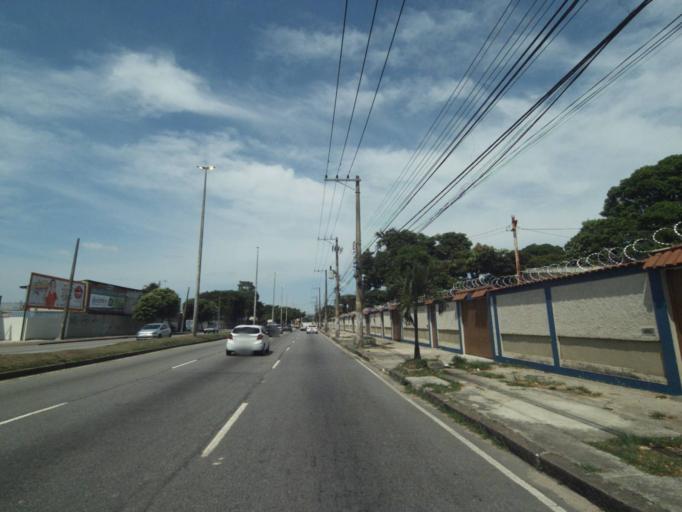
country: BR
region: Rio de Janeiro
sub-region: Rio De Janeiro
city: Rio de Janeiro
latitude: -22.8186
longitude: -43.2255
